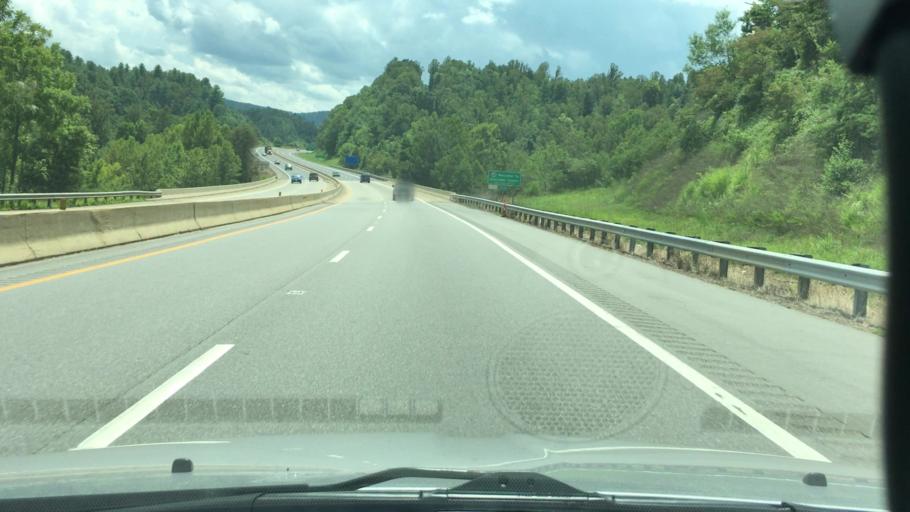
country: US
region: North Carolina
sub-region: Madison County
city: Mars Hill
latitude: 35.7930
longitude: -82.5398
